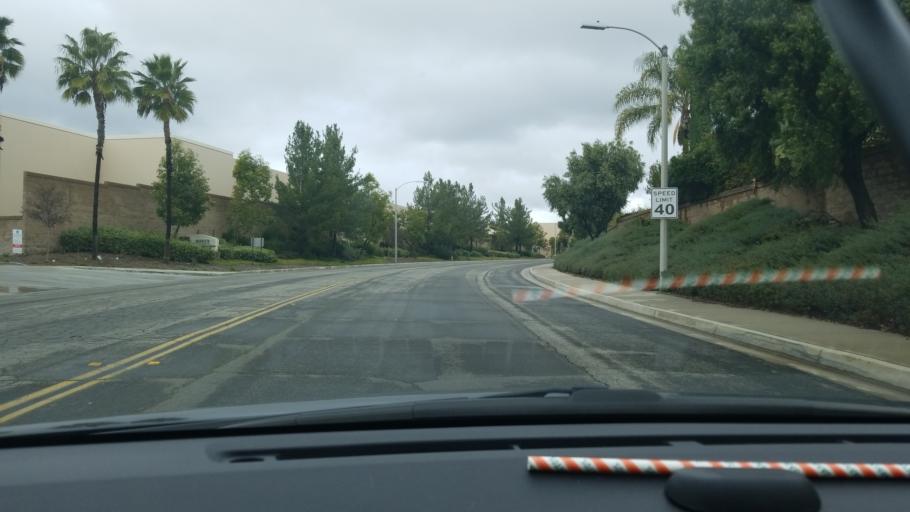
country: US
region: California
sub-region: Riverside County
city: Murrieta Hot Springs
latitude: 33.5675
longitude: -117.1790
